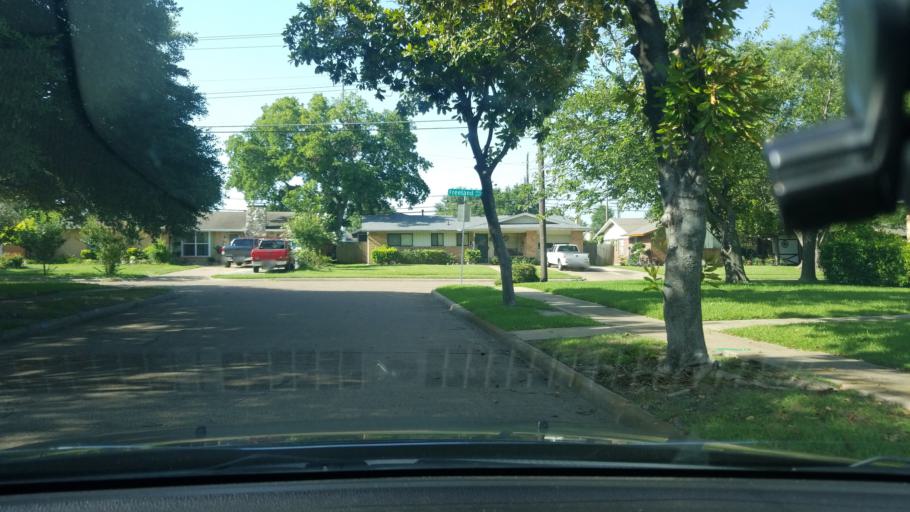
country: US
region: Texas
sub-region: Dallas County
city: Mesquite
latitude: 32.8079
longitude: -96.6793
